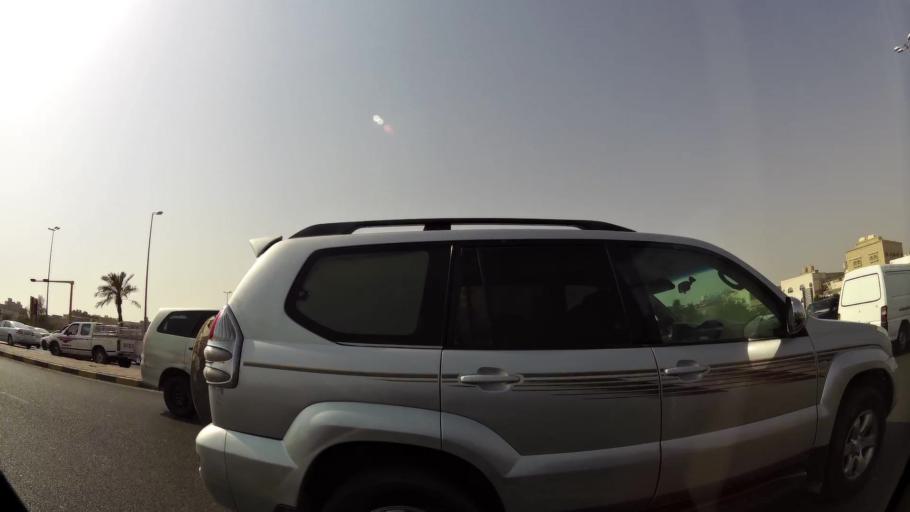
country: KW
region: Muhafazat al Jahra'
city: Al Jahra'
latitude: 29.3364
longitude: 47.6665
